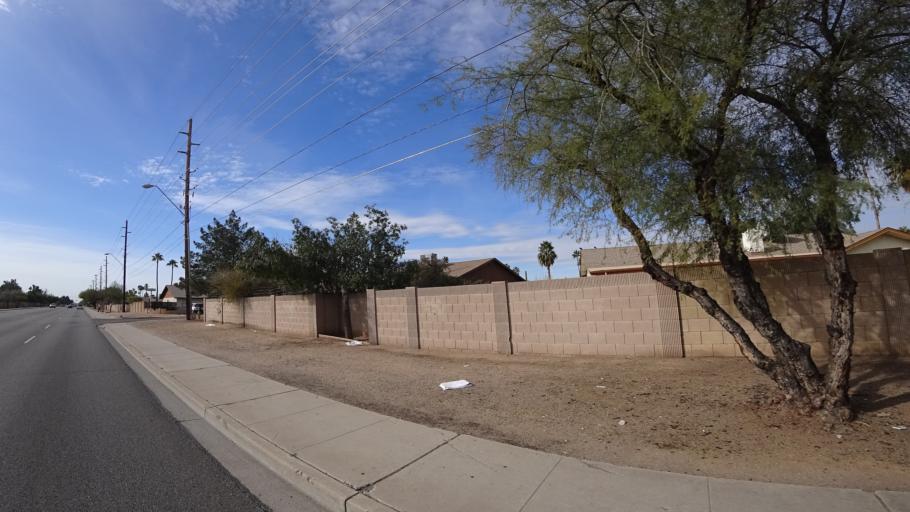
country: US
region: Arizona
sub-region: Maricopa County
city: Glendale
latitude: 33.5935
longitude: -112.1515
